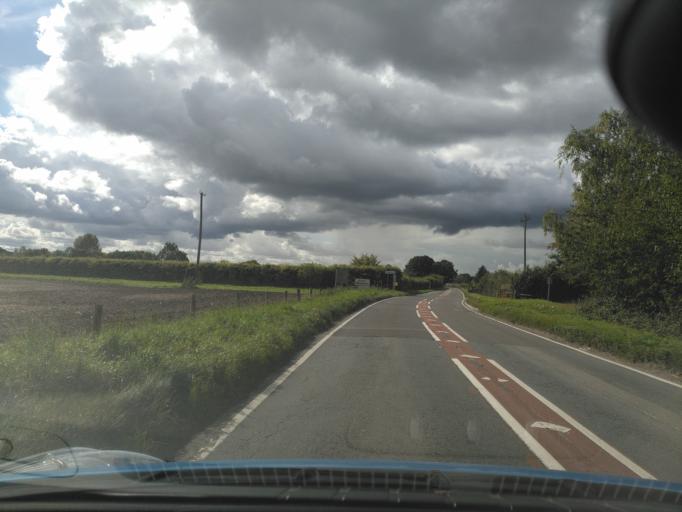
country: GB
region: England
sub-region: Oxfordshire
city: Harwell
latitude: 51.6007
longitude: -1.3297
